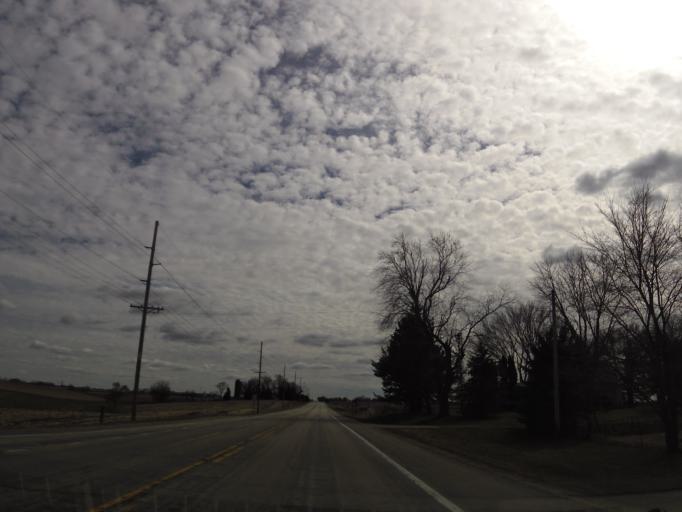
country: US
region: Minnesota
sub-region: Olmsted County
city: Rochester
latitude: 43.9412
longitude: -92.4087
